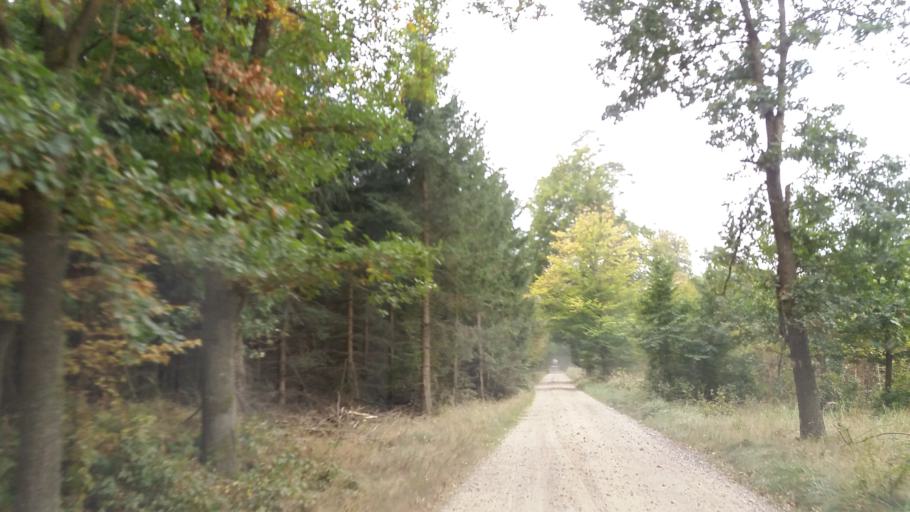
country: PL
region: West Pomeranian Voivodeship
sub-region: Powiat mysliborski
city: Barlinek
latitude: 52.9167
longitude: 15.2037
